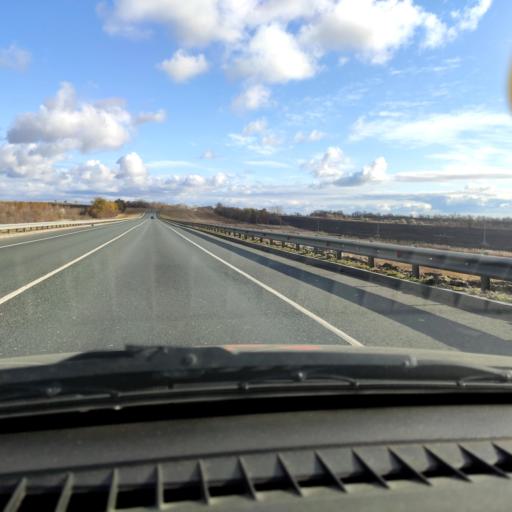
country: RU
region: Samara
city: Balasheyka
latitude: 53.1906
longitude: 48.2161
